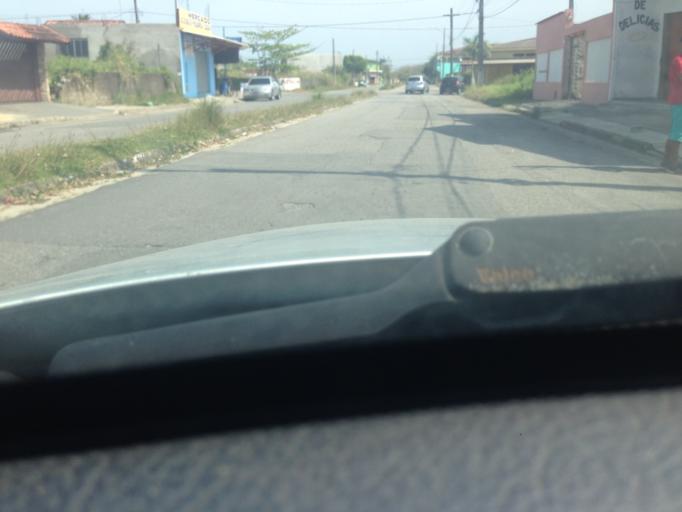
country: BR
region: Sao Paulo
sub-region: Itanhaem
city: Itanhaem
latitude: -24.2281
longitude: -46.8709
